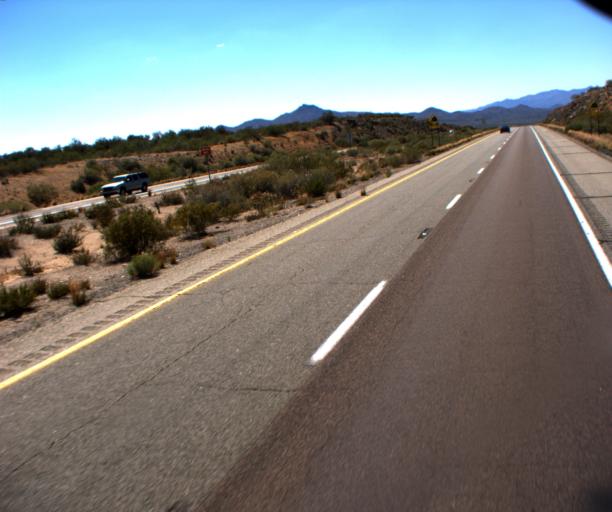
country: US
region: Arizona
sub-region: Yavapai County
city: Bagdad
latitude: 34.4914
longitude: -113.3853
